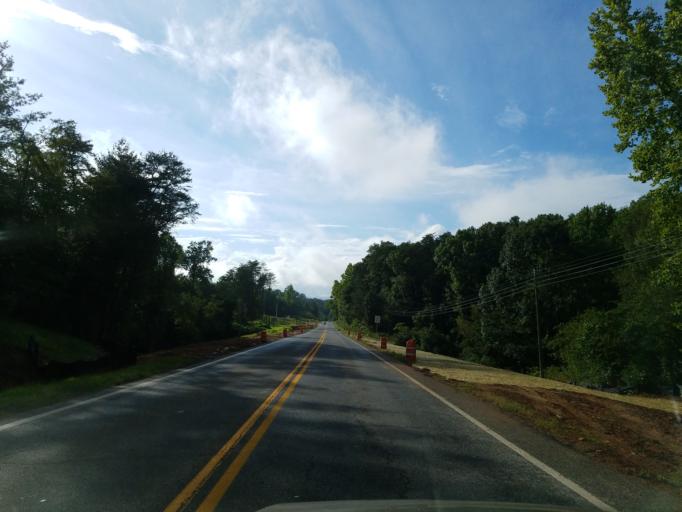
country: US
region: Georgia
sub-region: White County
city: Cleveland
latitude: 34.6086
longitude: -83.7718
